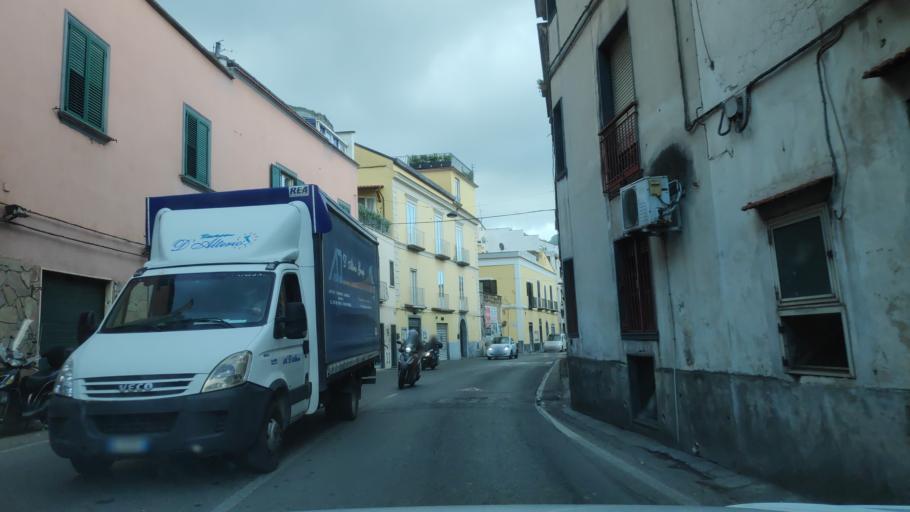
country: IT
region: Campania
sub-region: Provincia di Napoli
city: Meta
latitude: 40.6433
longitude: 14.4169
